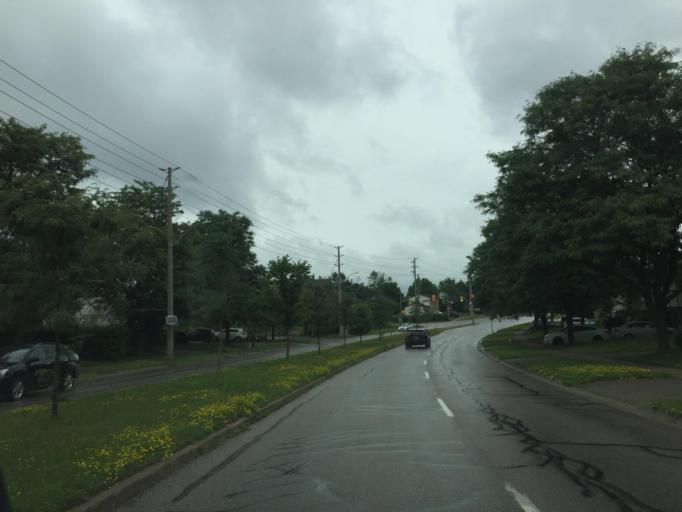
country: CA
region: Ontario
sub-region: Wellington County
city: Guelph
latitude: 43.5096
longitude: -80.2299
